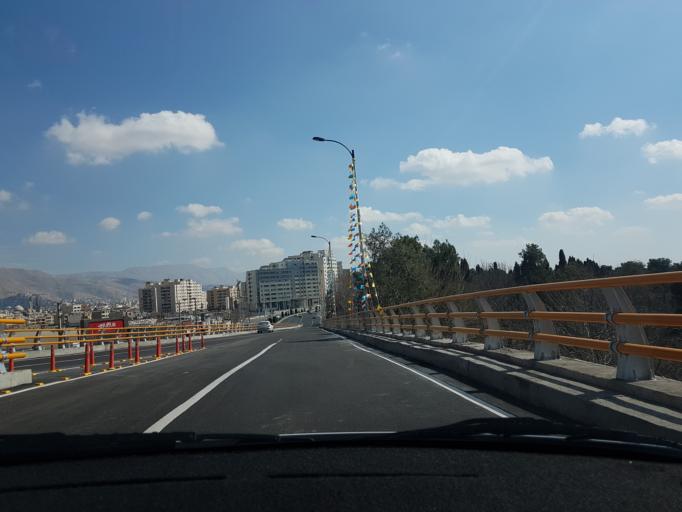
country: IR
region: Fars
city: Shiraz
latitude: 29.6155
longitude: 52.4688
